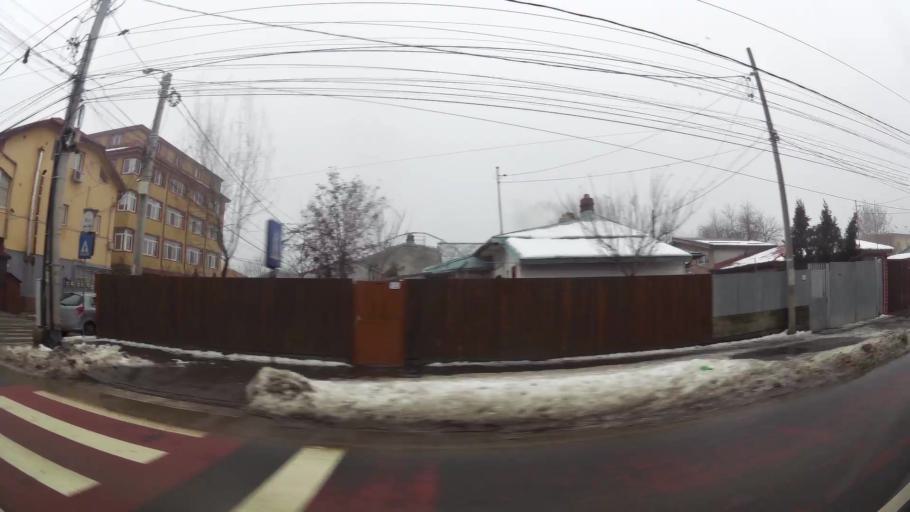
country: RO
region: Ilfov
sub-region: Comuna Chiajna
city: Rosu
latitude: 44.4717
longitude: 26.0193
